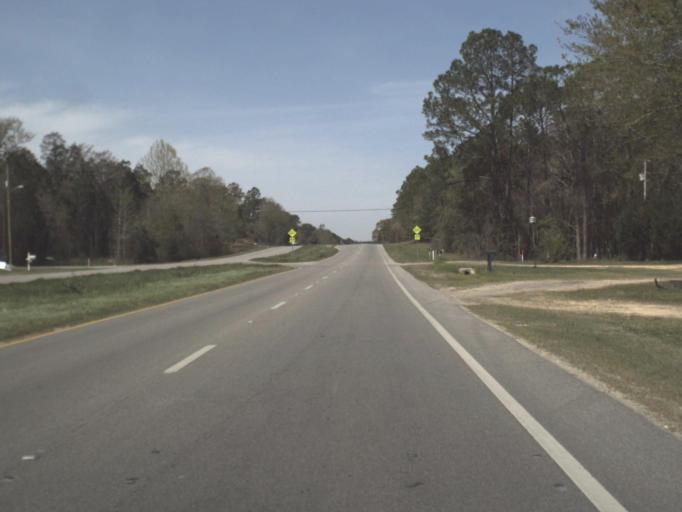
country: US
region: Florida
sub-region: Holmes County
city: Bonifay
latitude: 30.7888
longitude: -85.6918
